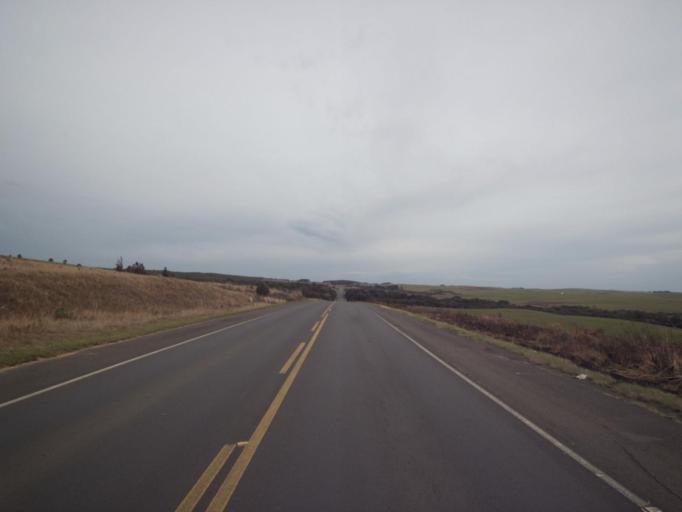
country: BR
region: Parana
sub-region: Palmas
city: Palmas
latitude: -26.7322
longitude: -51.6443
